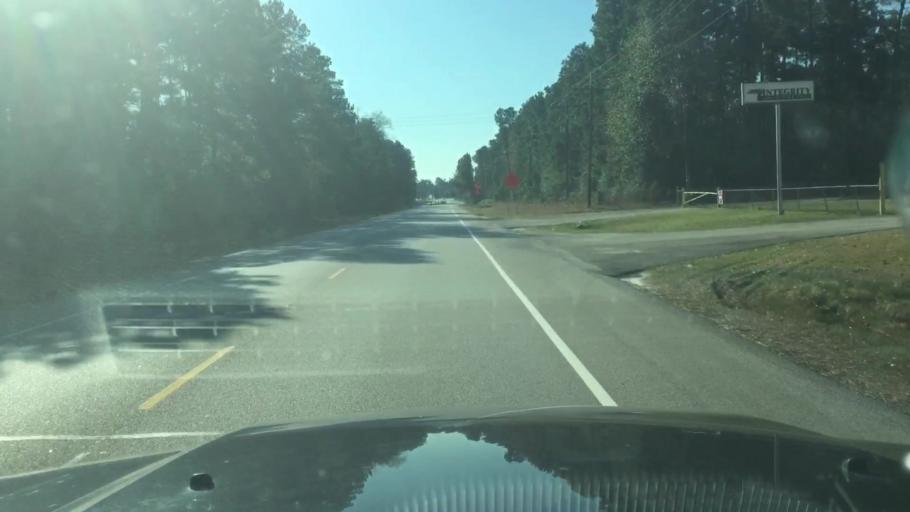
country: US
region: Texas
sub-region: Montgomery County
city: Porter Heights
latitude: 30.2205
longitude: -95.3600
